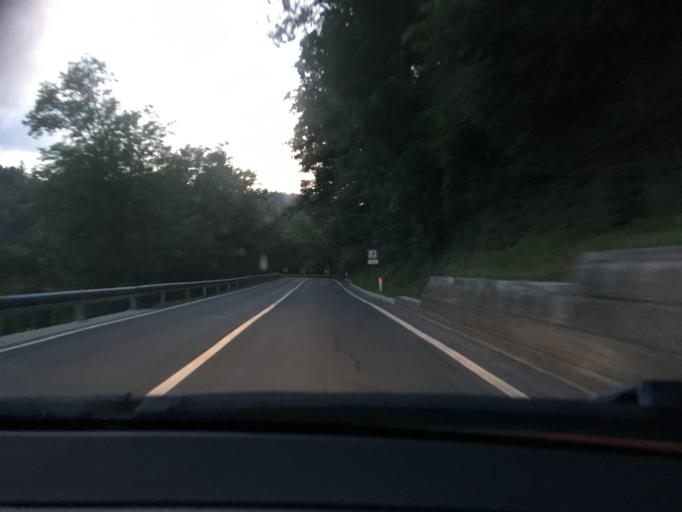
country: SI
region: Pivka
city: Pivka
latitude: 45.6183
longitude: 14.1684
